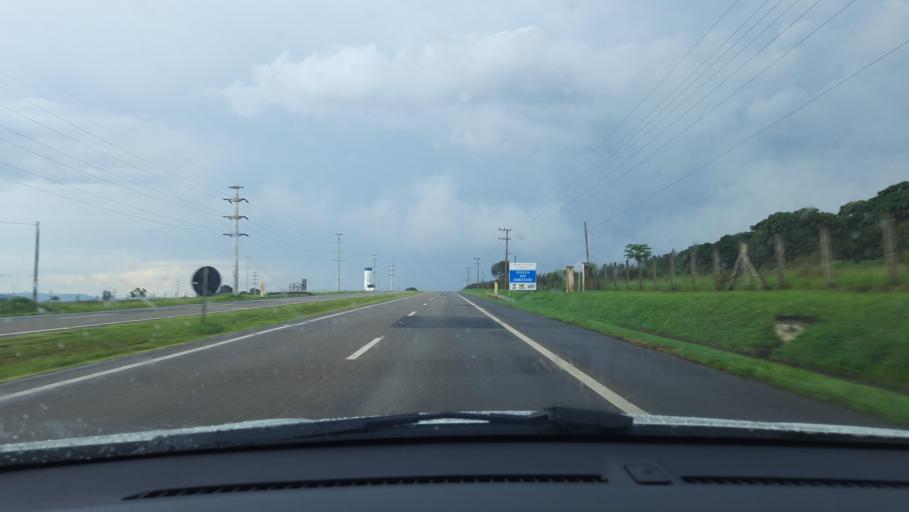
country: BR
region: Sao Paulo
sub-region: Casa Branca
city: Casa Branca
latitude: -21.7621
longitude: -47.0700
